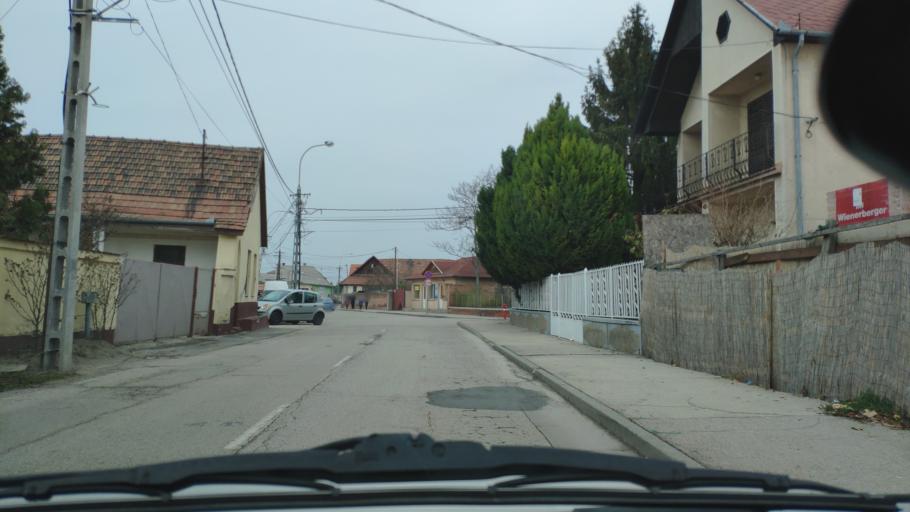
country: HU
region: Pest
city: Szigetszentmiklos
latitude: 47.3471
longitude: 19.0463
